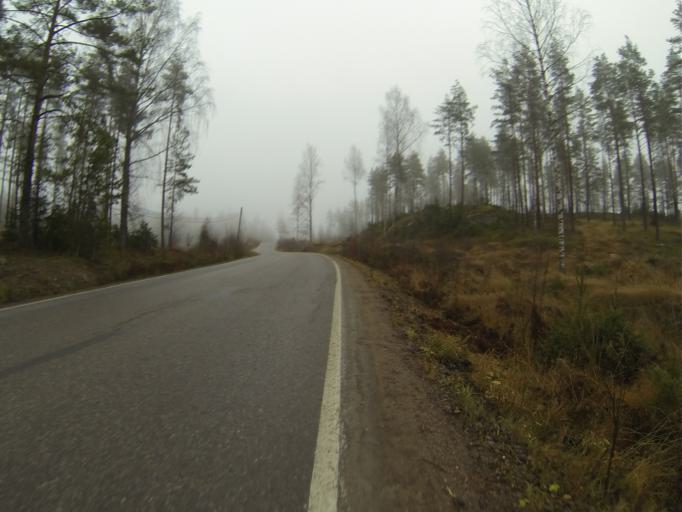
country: FI
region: Varsinais-Suomi
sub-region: Salo
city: Halikko
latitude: 60.4160
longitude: 22.9363
